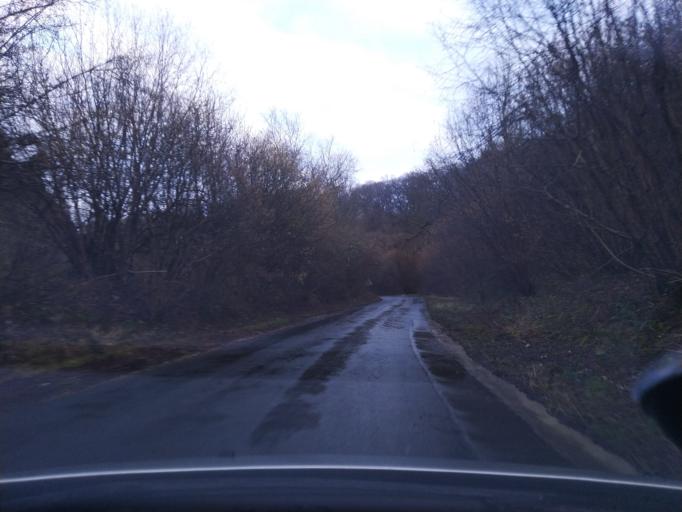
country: FR
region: Haute-Normandie
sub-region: Departement de la Seine-Maritime
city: Duclair
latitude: 49.4887
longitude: 0.8995
